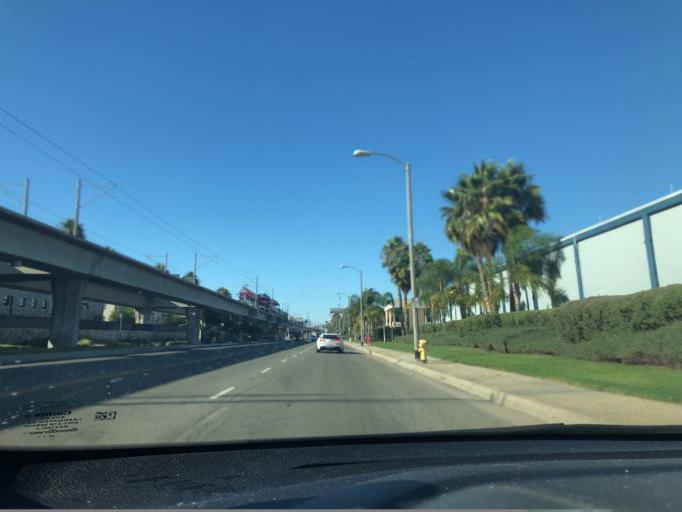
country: US
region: California
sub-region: Los Angeles County
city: Del Aire
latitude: 33.9212
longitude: -118.3874
